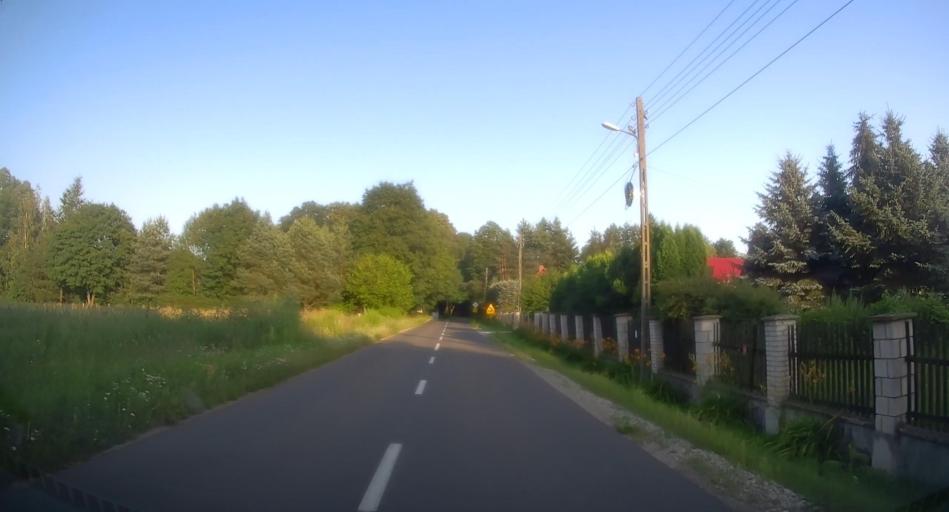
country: PL
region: Lodz Voivodeship
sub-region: Powiat skierniewicki
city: Kowiesy
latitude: 51.8921
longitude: 20.3866
